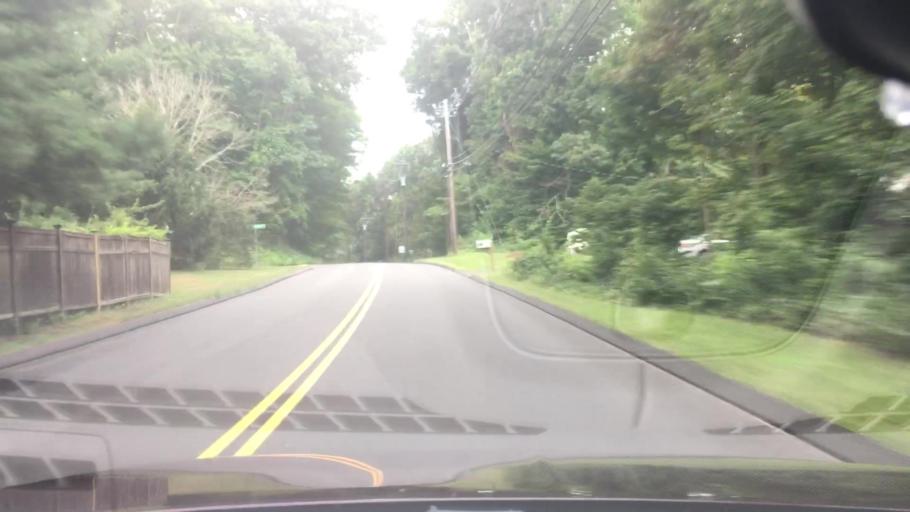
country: US
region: Connecticut
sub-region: New Haven County
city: Madison
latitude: 41.3078
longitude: -72.6001
